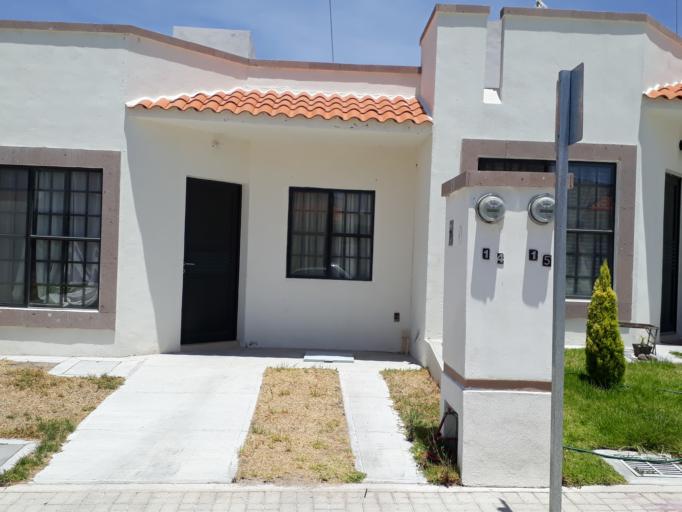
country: MX
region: Aguascalientes
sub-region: Aguascalientes
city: San Sebastian [Fraccionamiento]
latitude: 21.8115
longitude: -102.3044
